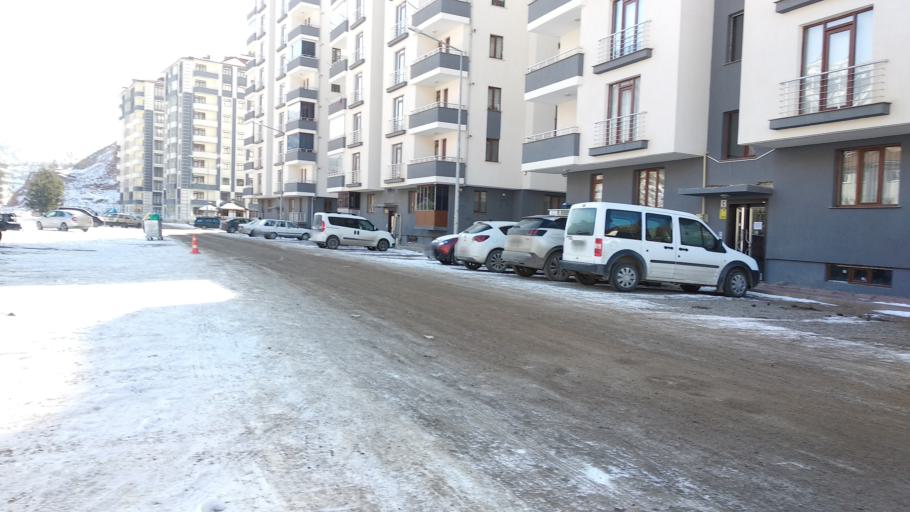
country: TR
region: Gumushane
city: Gumushkhane
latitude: 40.4517
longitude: 39.4922
